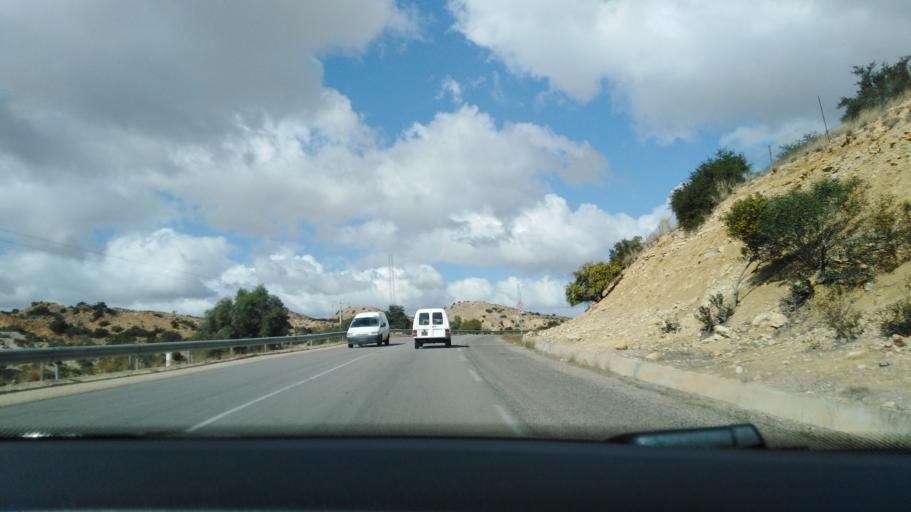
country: TN
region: Al Qayrawan
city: Haffouz
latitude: 35.6347
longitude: 9.8185
